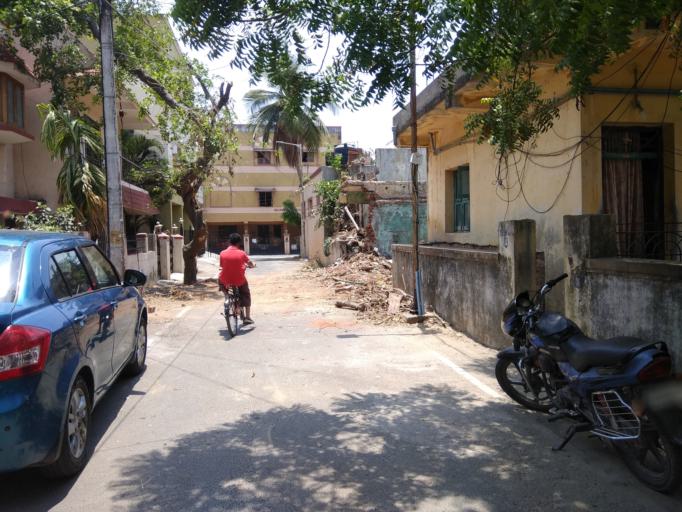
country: IN
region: Tamil Nadu
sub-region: Kancheepuram
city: Alandur
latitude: 12.9940
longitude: 80.2054
